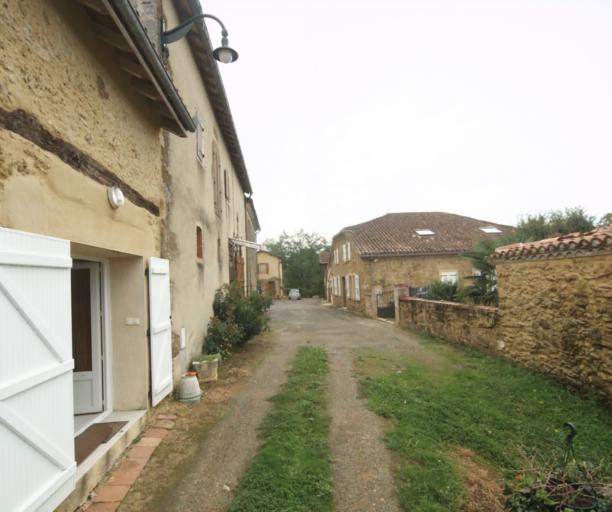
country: FR
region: Midi-Pyrenees
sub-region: Departement du Gers
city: Cazaubon
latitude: 43.9040
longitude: -0.1533
